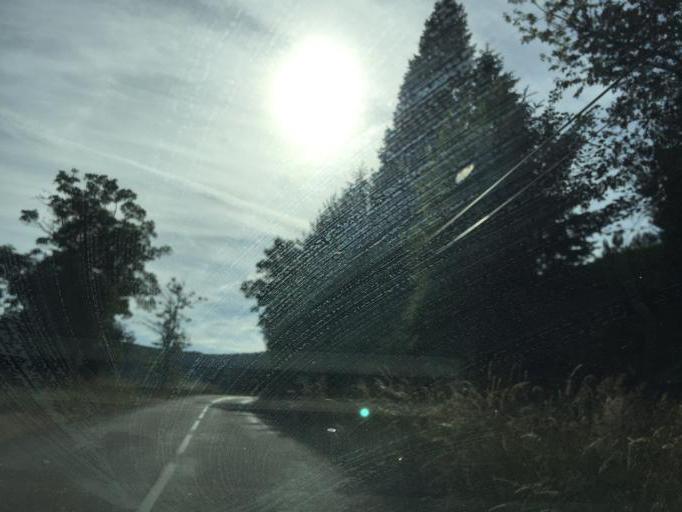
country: FR
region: Rhone-Alpes
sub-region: Departement de la Loire
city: Bourg-Argental
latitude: 45.3574
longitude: 4.5545
